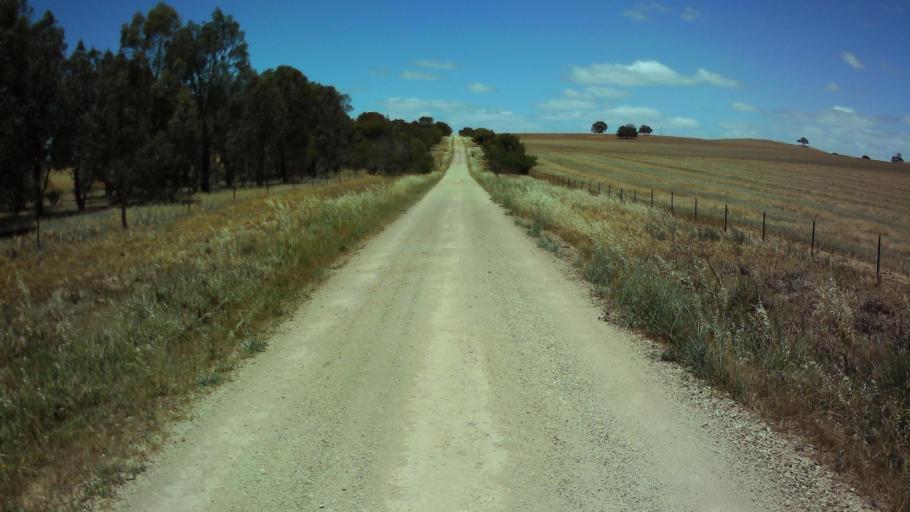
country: AU
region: New South Wales
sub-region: Weddin
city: Grenfell
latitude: -33.9432
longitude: 148.3708
